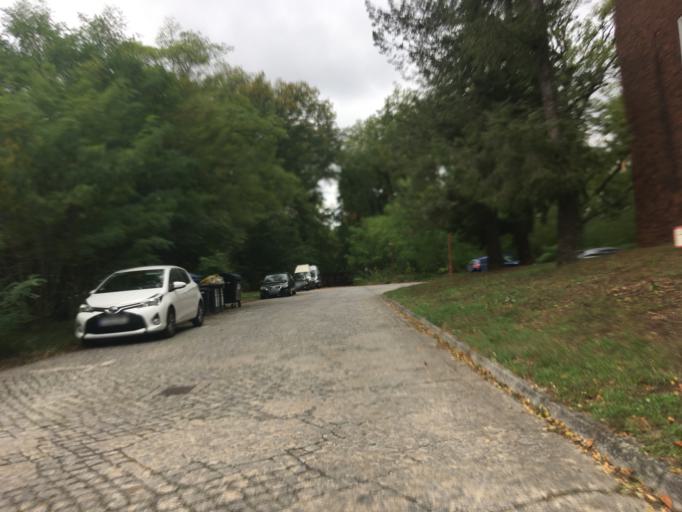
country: DE
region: Berlin
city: Kladow
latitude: 52.4814
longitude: 13.1238
